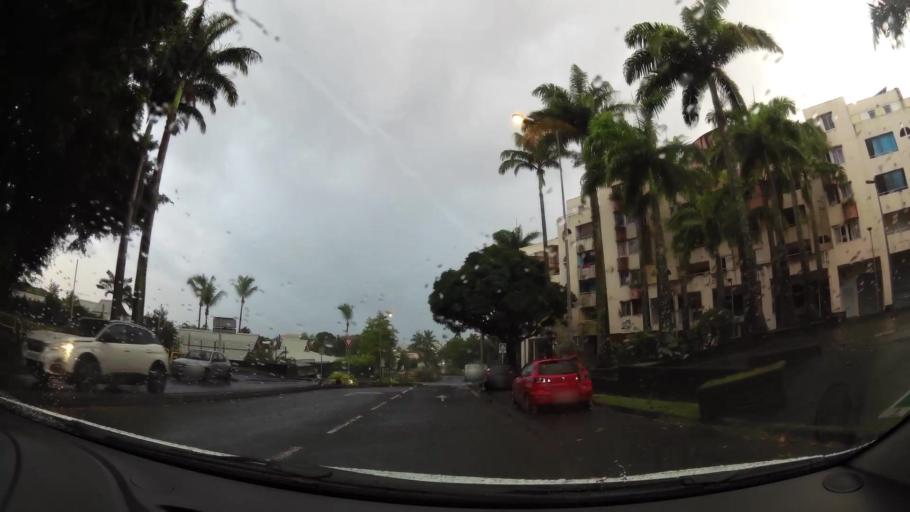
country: RE
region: Reunion
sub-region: Reunion
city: Saint-Benoit
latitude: -21.0392
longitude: 55.7106
